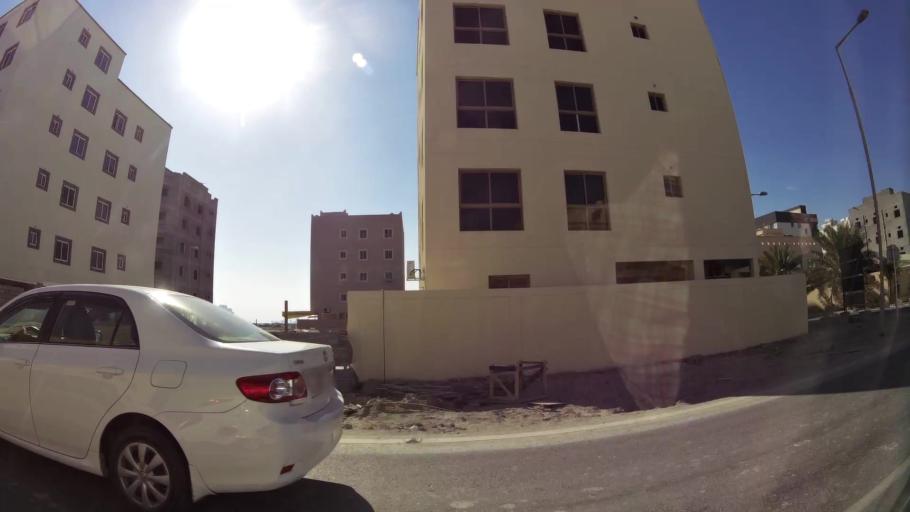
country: BH
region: Muharraq
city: Al Hadd
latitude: 26.2397
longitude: 50.6481
